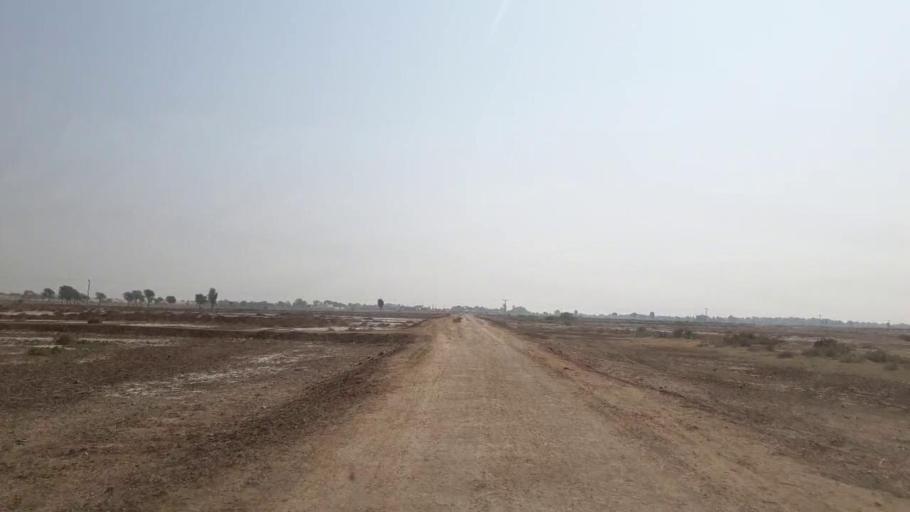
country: PK
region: Sindh
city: Mirpur Khas
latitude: 25.6444
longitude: 69.1417
